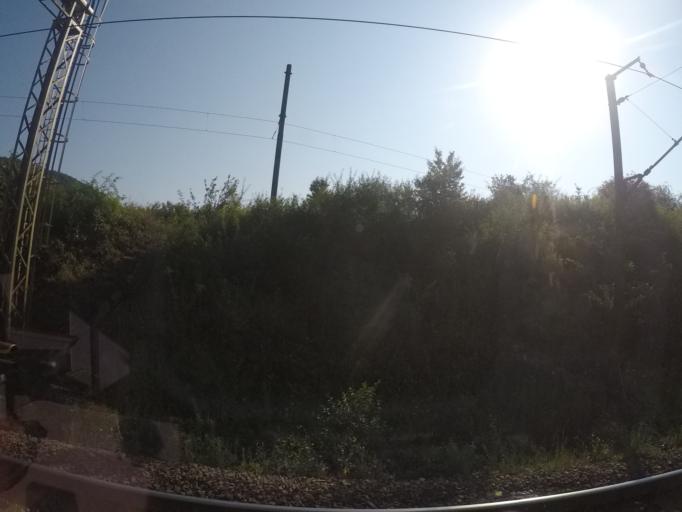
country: SK
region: Presovsky
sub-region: Okres Presov
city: Presov
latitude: 48.8589
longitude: 21.2224
